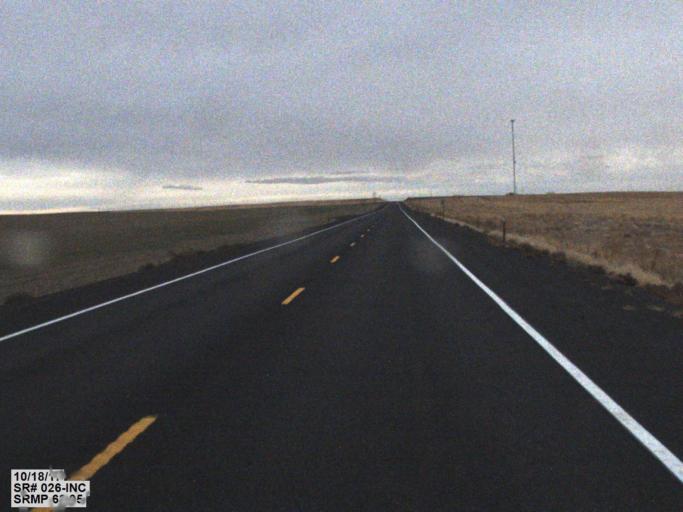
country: US
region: Washington
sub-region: Franklin County
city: Connell
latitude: 46.7944
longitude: -118.6874
